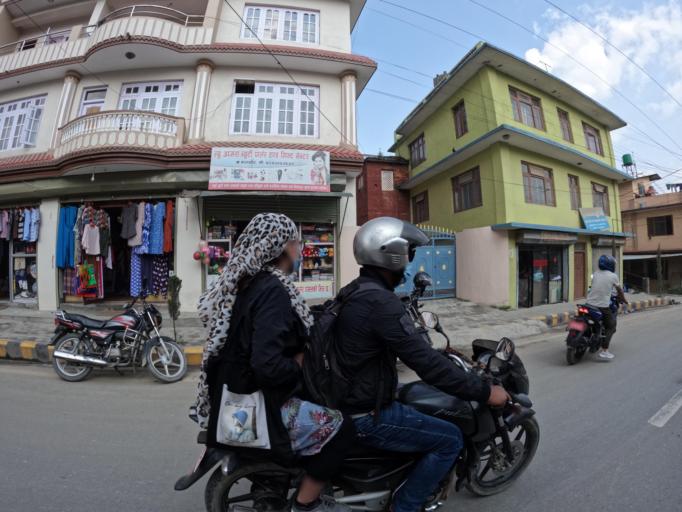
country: NP
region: Central Region
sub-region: Bagmati Zone
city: Patan
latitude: 27.6686
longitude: 85.3654
